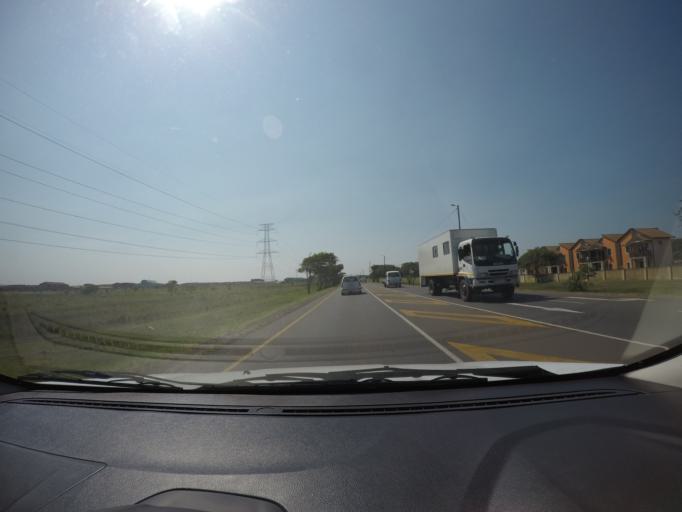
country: ZA
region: KwaZulu-Natal
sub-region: uThungulu District Municipality
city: Richards Bay
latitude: -28.7382
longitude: 32.0446
